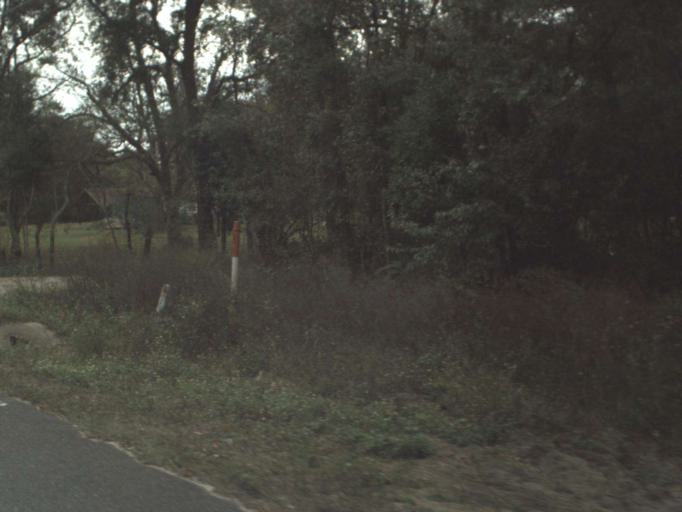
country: US
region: Florida
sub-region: Wakulla County
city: Crawfordville
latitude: 30.1139
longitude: -84.3827
